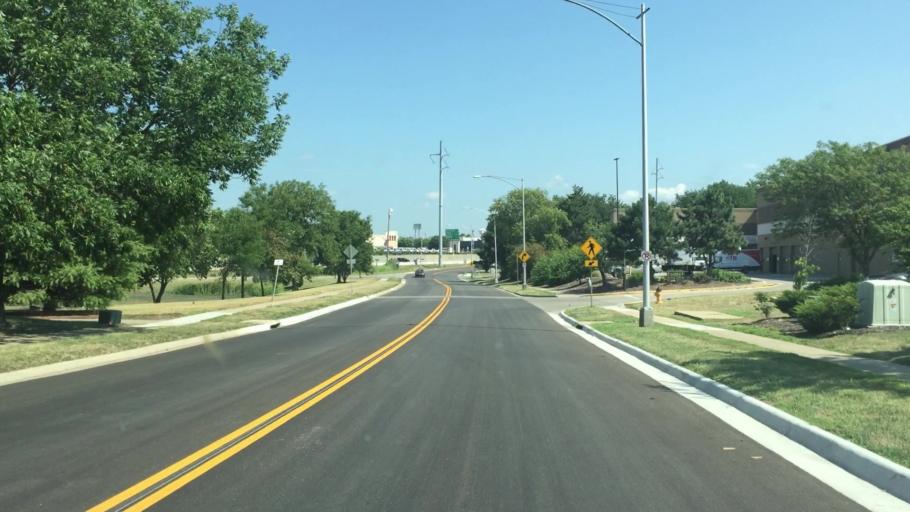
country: US
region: Kansas
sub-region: Johnson County
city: Lenexa
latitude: 38.9582
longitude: -94.7283
